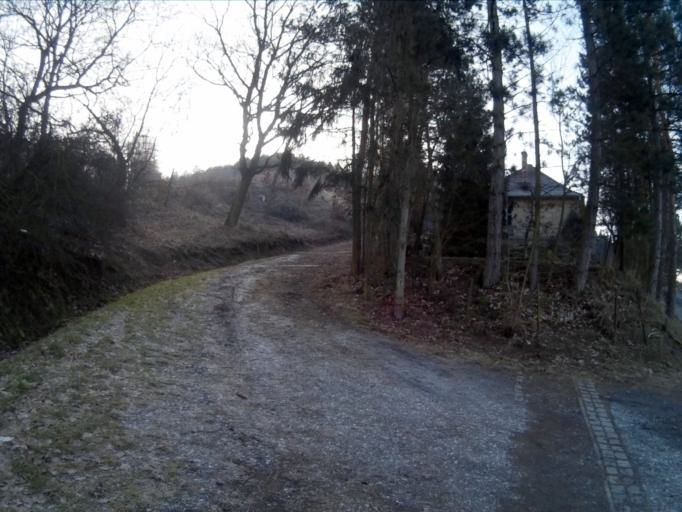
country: CZ
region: Vysocina
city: Namest' nad Oslavou
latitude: 49.2019
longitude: 16.1594
